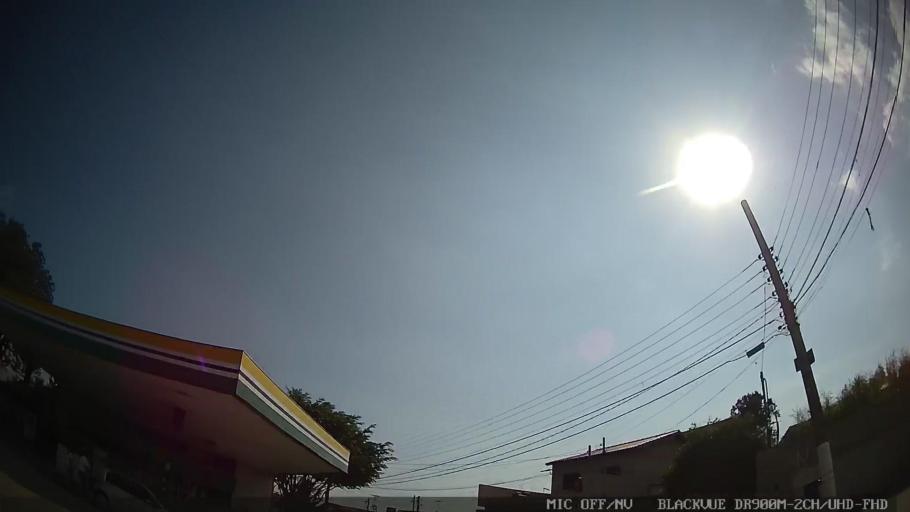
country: BR
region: Sao Paulo
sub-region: Ferraz De Vasconcelos
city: Ferraz de Vasconcelos
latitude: -23.5025
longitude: -46.4481
